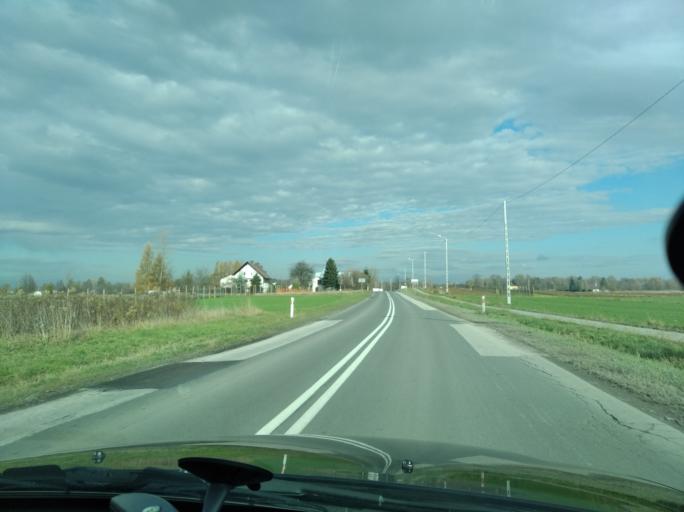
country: PL
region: Subcarpathian Voivodeship
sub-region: Powiat ropczycko-sedziszowski
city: Ostrow
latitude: 50.0903
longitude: 21.5917
